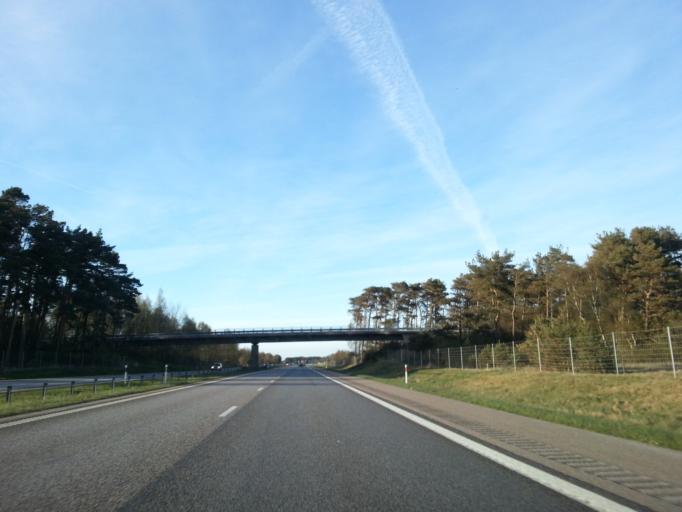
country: SE
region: Halland
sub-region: Laholms Kommun
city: Mellbystrand
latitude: 56.4843
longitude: 12.9492
